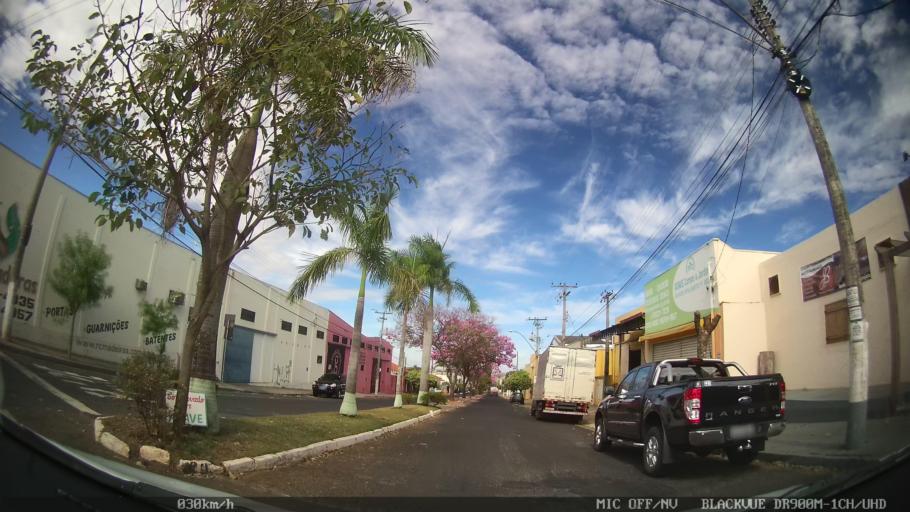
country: BR
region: Sao Paulo
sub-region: Bady Bassitt
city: Bady Bassitt
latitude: -20.8194
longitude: -49.5234
